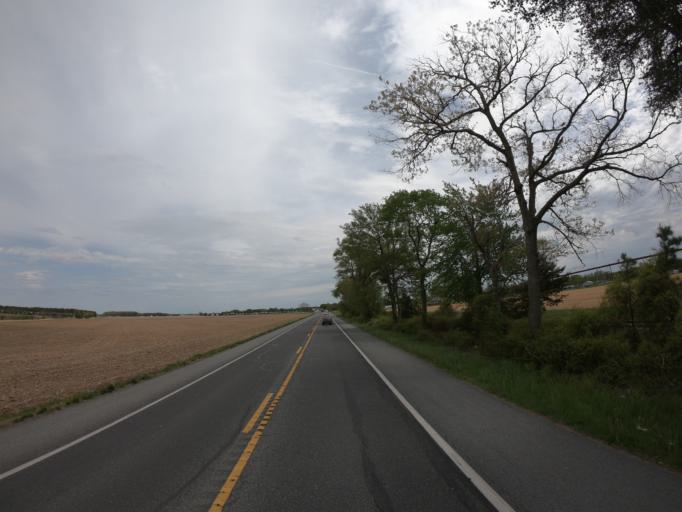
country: US
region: Delaware
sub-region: Sussex County
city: Milton
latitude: 38.7865
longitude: -75.3624
